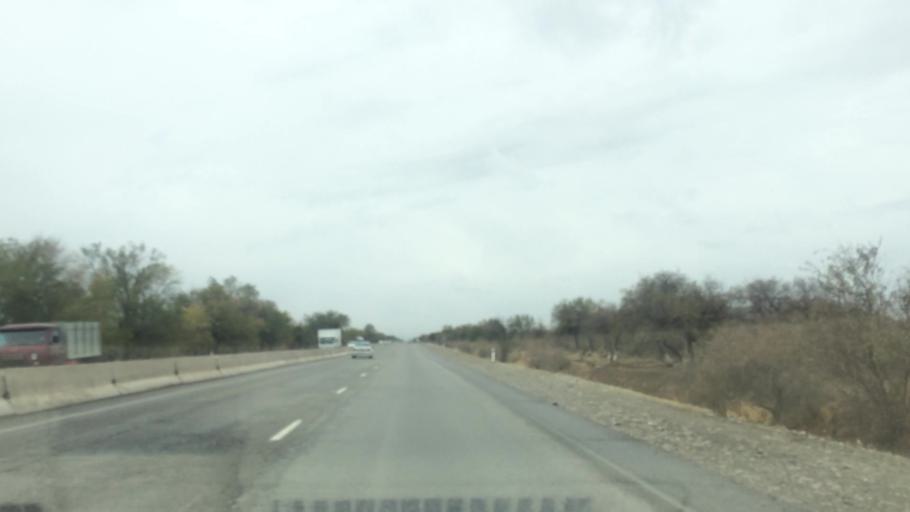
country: UZ
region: Samarqand
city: Bulung'ur
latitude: 39.8199
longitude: 67.3876
